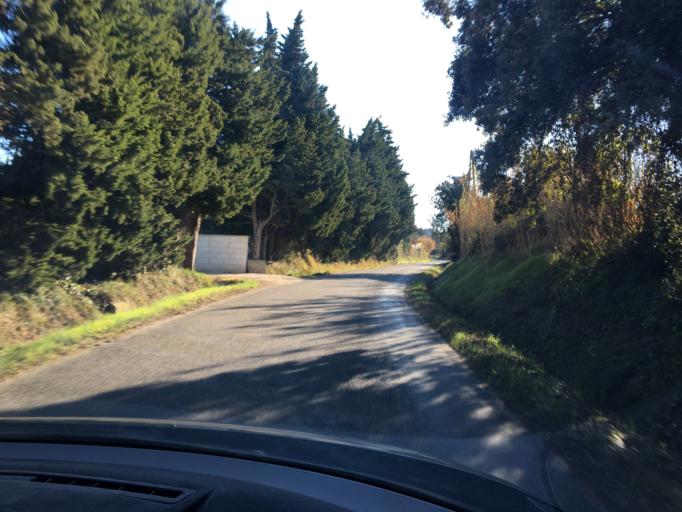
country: FR
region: Provence-Alpes-Cote d'Azur
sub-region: Departement des Bouches-du-Rhone
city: Saint-Remy-de-Provence
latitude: 43.7863
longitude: 4.7922
